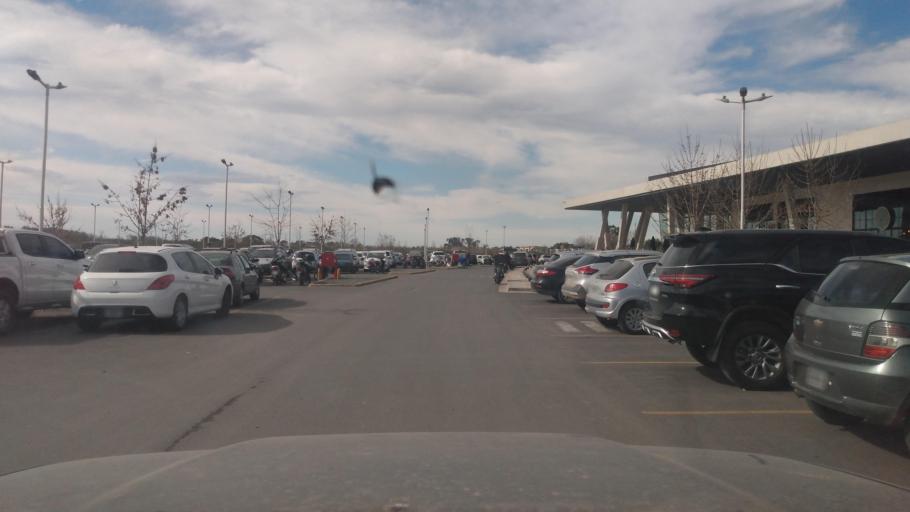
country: AR
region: Buenos Aires
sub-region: Partido de Lujan
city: Lujan
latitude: -34.5464
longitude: -59.1104
